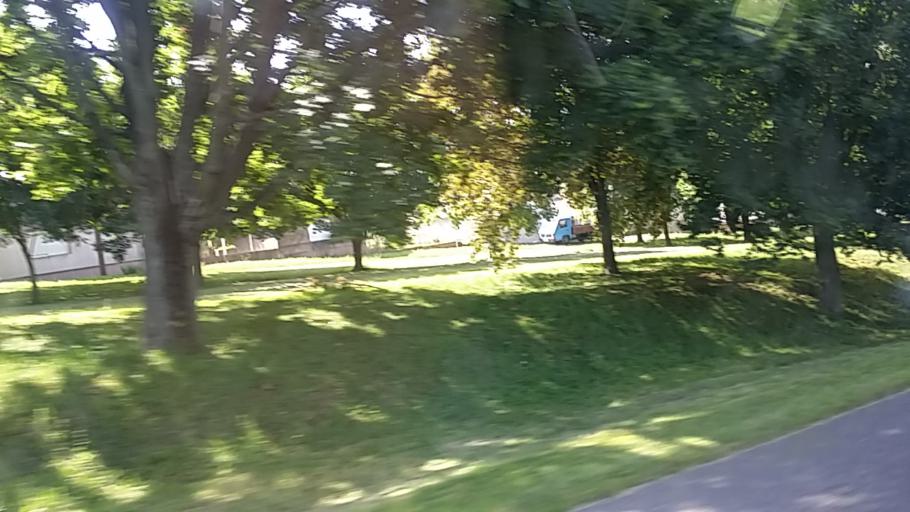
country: HU
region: Baranya
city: Siklos
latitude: 45.9084
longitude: 18.3349
